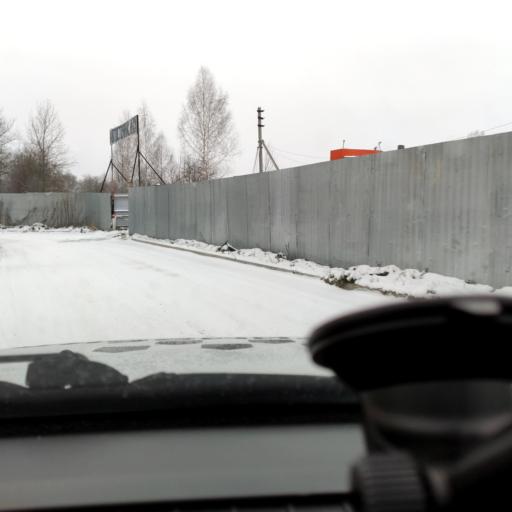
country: RU
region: Perm
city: Perm
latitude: 58.0509
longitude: 56.3463
